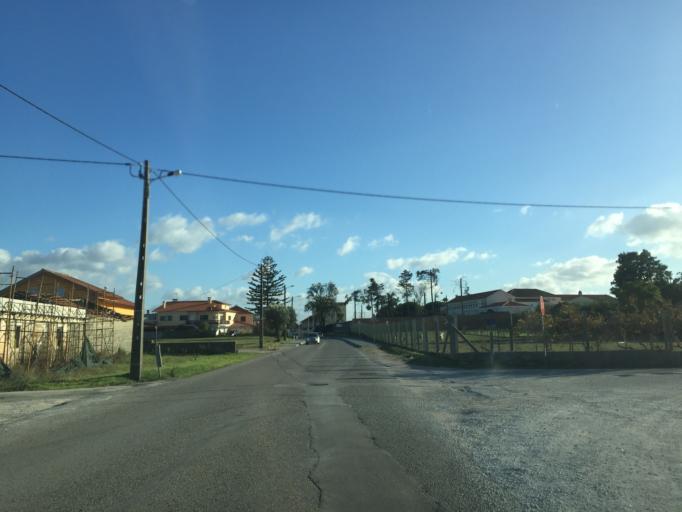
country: PT
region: Leiria
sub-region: Pombal
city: Lourical
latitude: 39.9546
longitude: -8.7863
